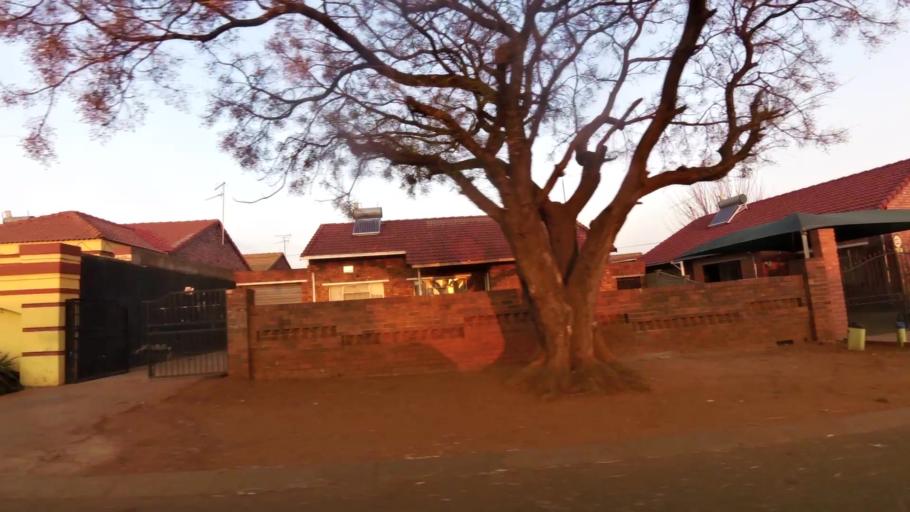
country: ZA
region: Gauteng
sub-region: City of Johannesburg Metropolitan Municipality
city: Soweto
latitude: -26.2891
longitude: 27.8893
